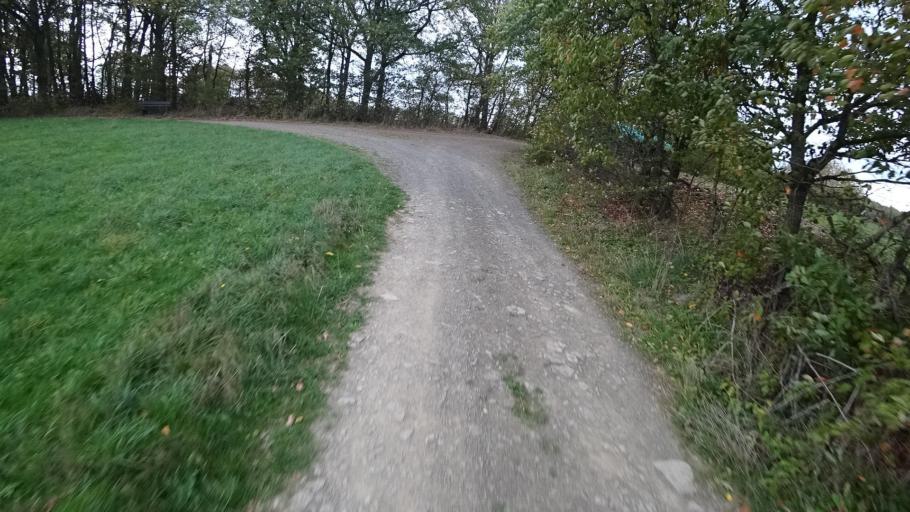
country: DE
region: Rheinland-Pfalz
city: Berg
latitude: 50.5543
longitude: 6.9266
